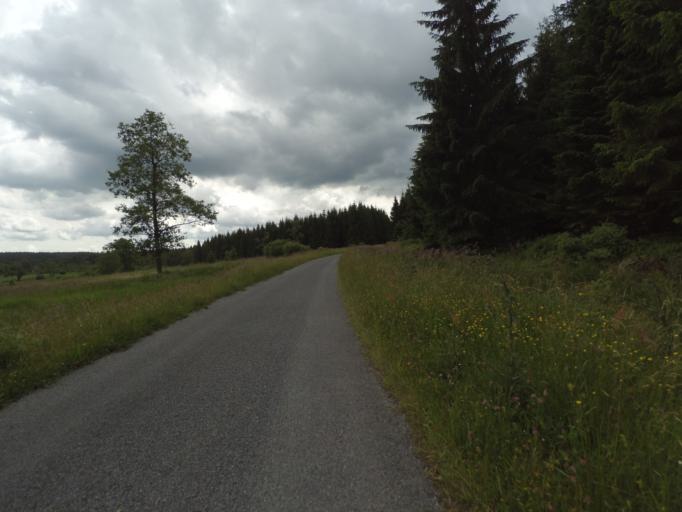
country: DE
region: North Rhine-Westphalia
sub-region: Regierungsbezirk Koln
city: Monschau
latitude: 50.5825
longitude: 6.1802
